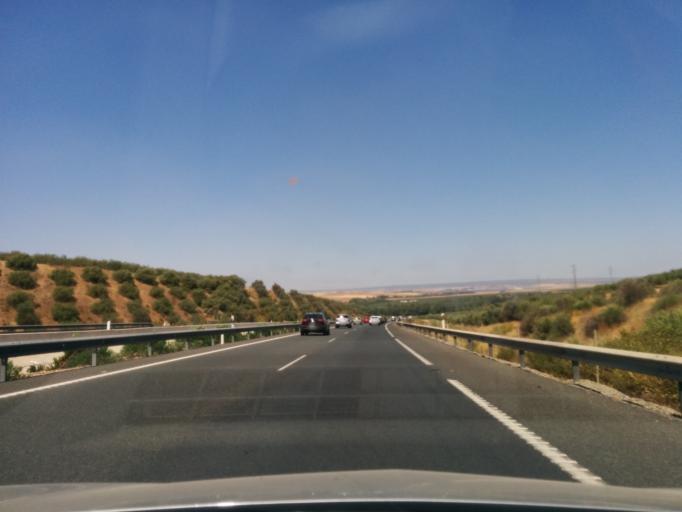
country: ES
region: Andalusia
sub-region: Provincia de Sevilla
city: Benacazon
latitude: 37.3655
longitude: -6.2134
